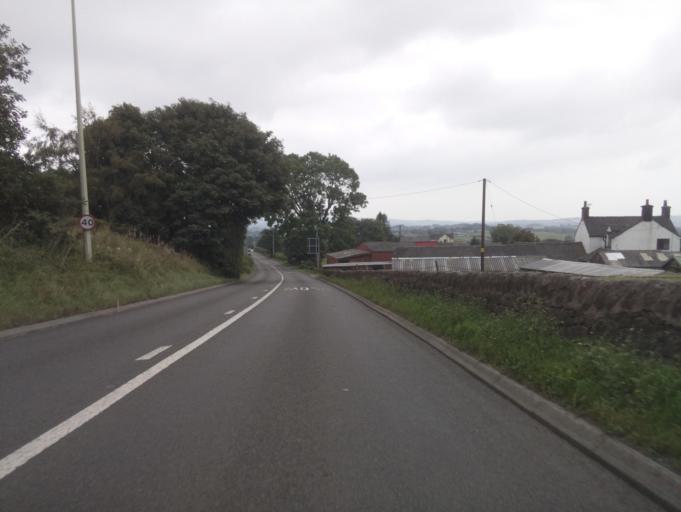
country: GB
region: England
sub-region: Staffordshire
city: Cheddleton
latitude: 53.0211
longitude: -2.0470
